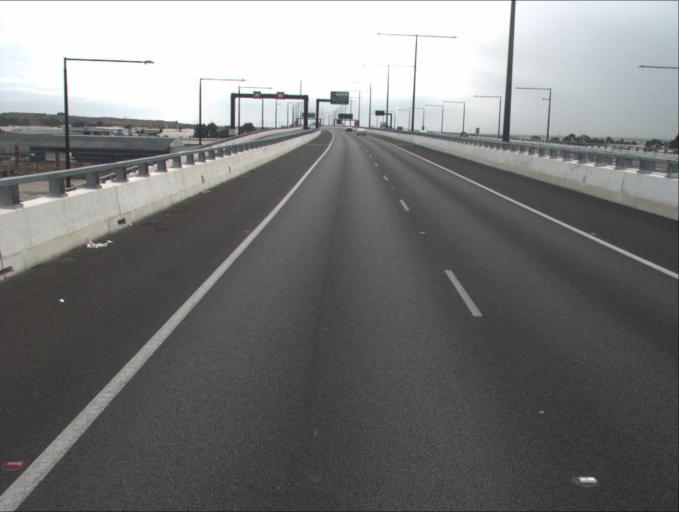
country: AU
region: South Australia
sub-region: Charles Sturt
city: Woodville North
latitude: -34.8460
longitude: 138.5643
